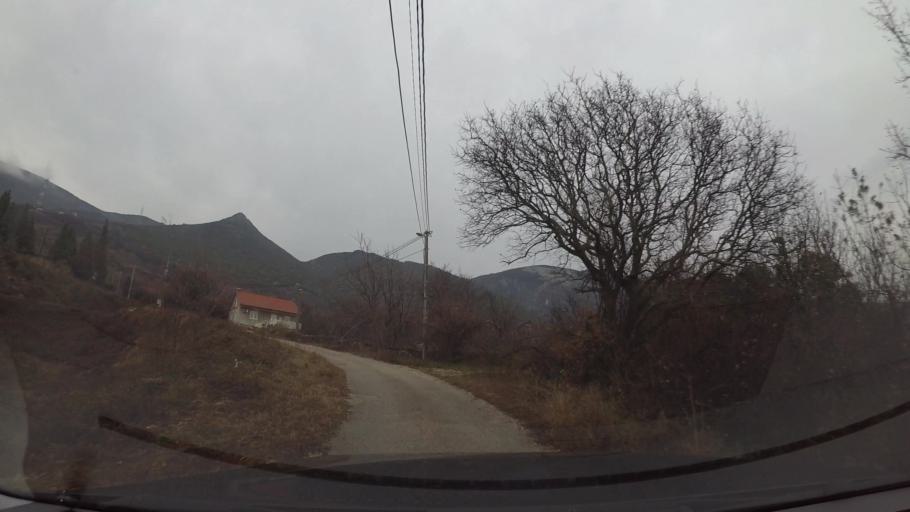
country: BA
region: Federation of Bosnia and Herzegovina
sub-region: Hercegovacko-Bosanski Kanton
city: Mostar
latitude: 43.3656
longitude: 17.8019
